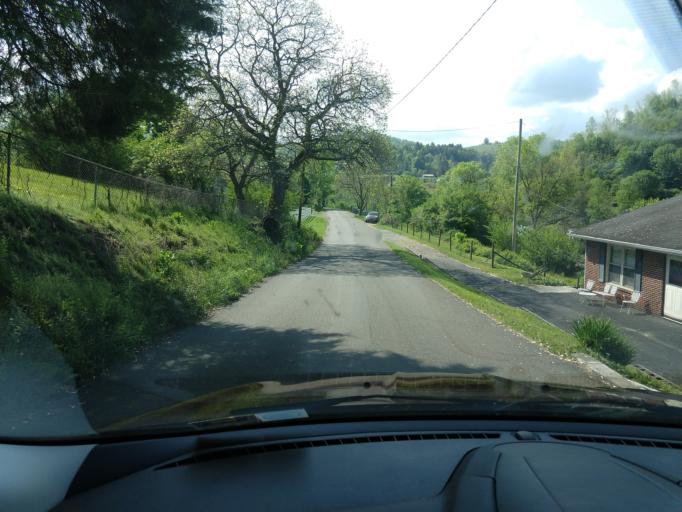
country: US
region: Virginia
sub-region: Russell County
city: Honaker
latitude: 37.0182
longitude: -81.9712
